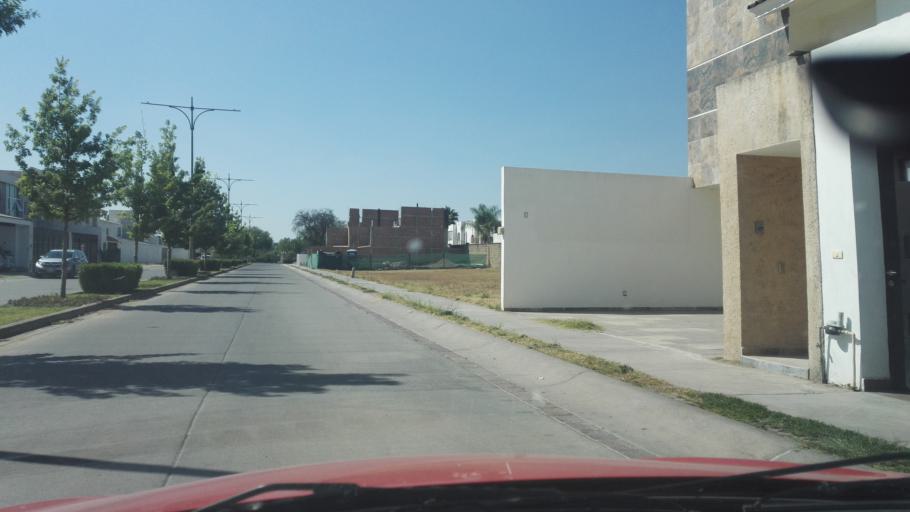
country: MX
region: Guanajuato
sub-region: Leon
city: Medina
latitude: 21.1257
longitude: -101.6095
